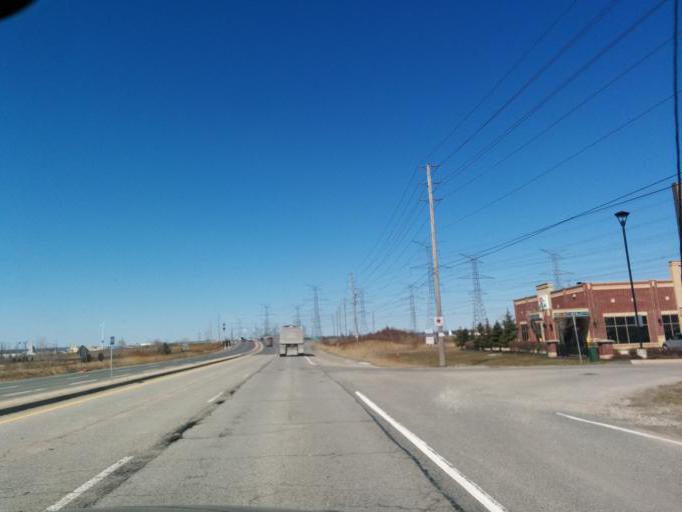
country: CA
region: Ontario
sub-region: Halton
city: Milton
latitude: 43.5391
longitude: -79.8579
